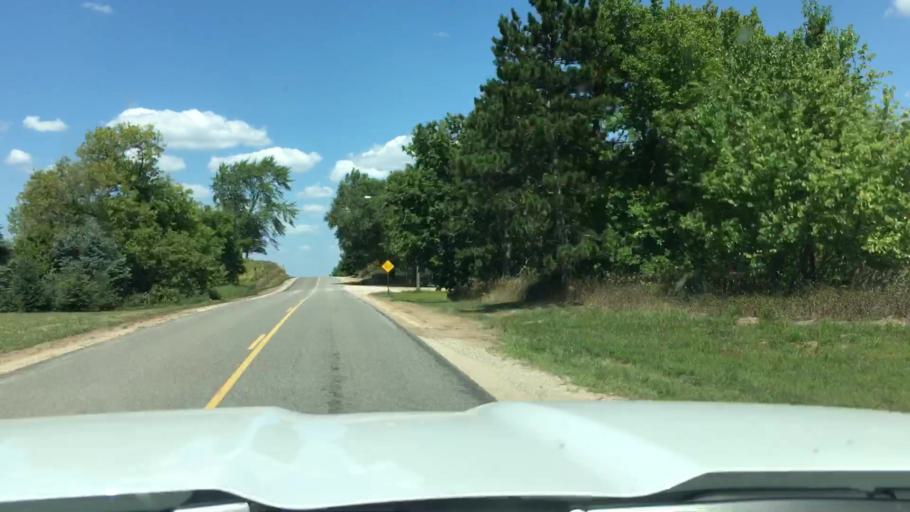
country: US
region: Michigan
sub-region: Muskegon County
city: Ravenna
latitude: 43.2602
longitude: -85.9180
